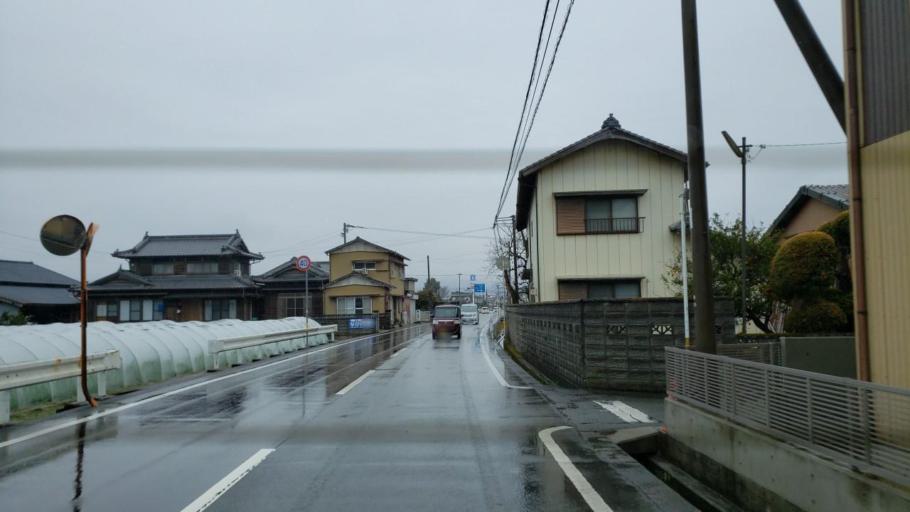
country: JP
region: Tokushima
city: Ishii
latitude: 34.1005
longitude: 134.4070
